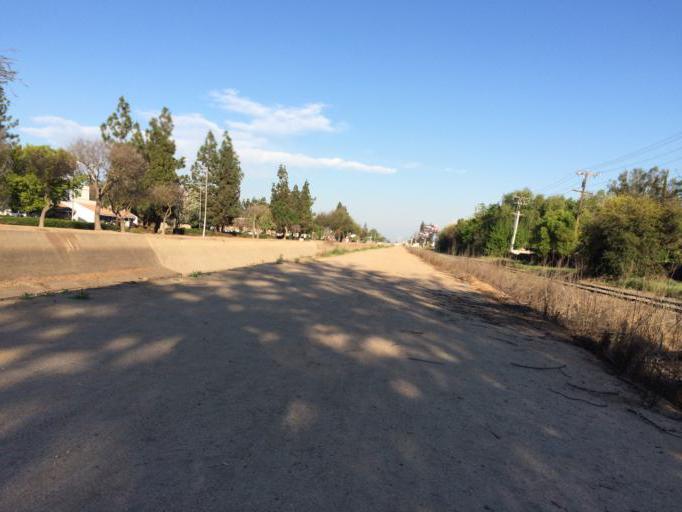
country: US
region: California
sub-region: Fresno County
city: Sunnyside
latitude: 36.7648
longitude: -119.7241
